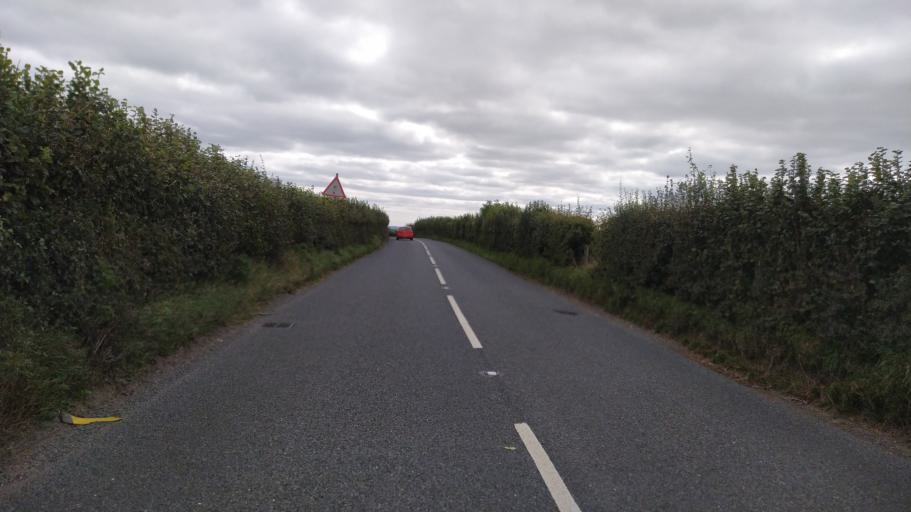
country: GB
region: England
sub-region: Somerset
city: Wincanton
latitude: 51.0647
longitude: -2.3510
